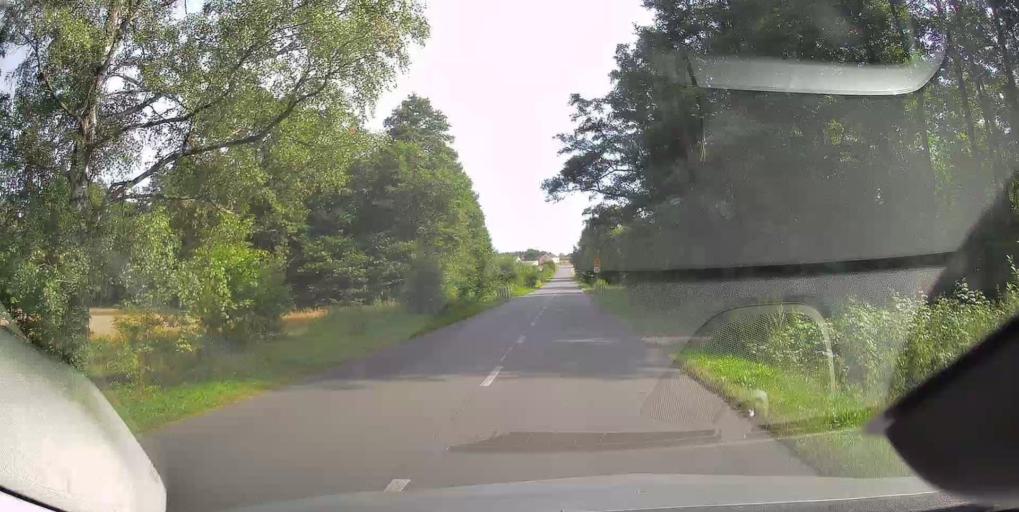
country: PL
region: Lodz Voivodeship
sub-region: Powiat opoczynski
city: Mniszkow
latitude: 51.4300
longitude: 20.0251
